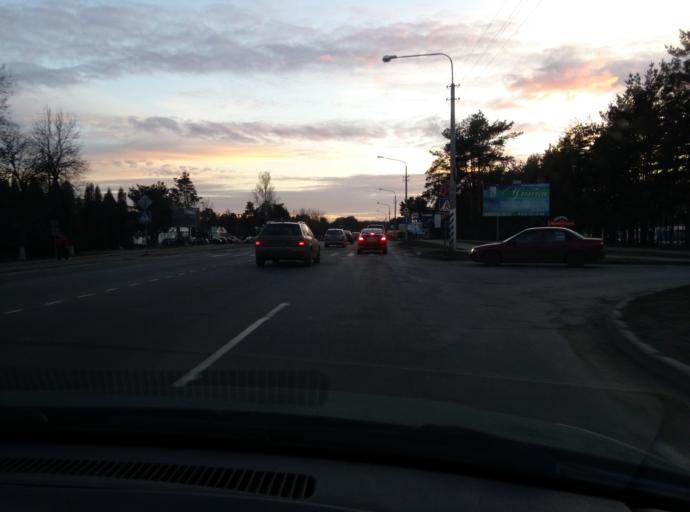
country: BY
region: Minsk
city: Horad Barysaw
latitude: 54.2110
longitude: 28.4868
